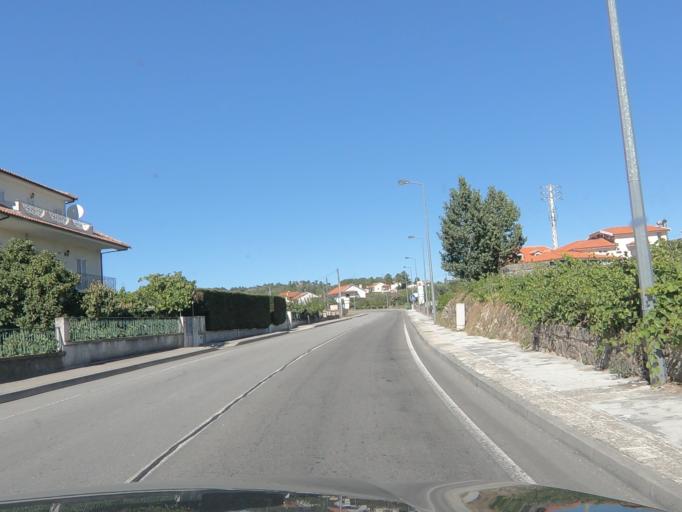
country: PT
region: Vila Real
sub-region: Valpacos
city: Valpacos
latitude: 41.6215
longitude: -7.3124
